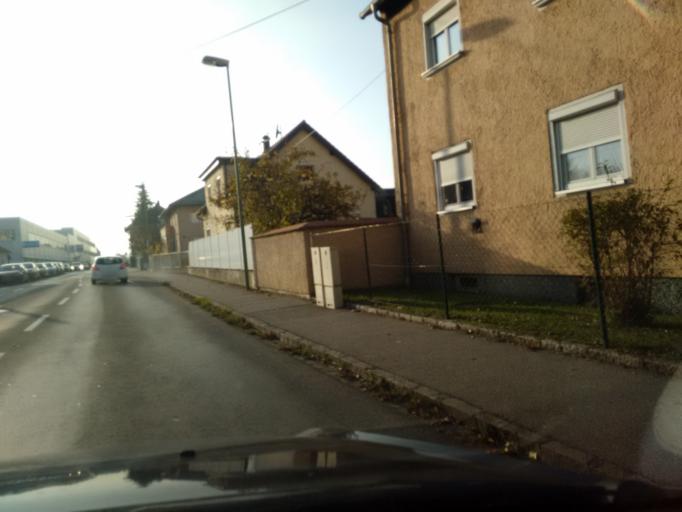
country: AT
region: Upper Austria
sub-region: Wels Stadt
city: Wels
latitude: 48.1743
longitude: 14.0224
